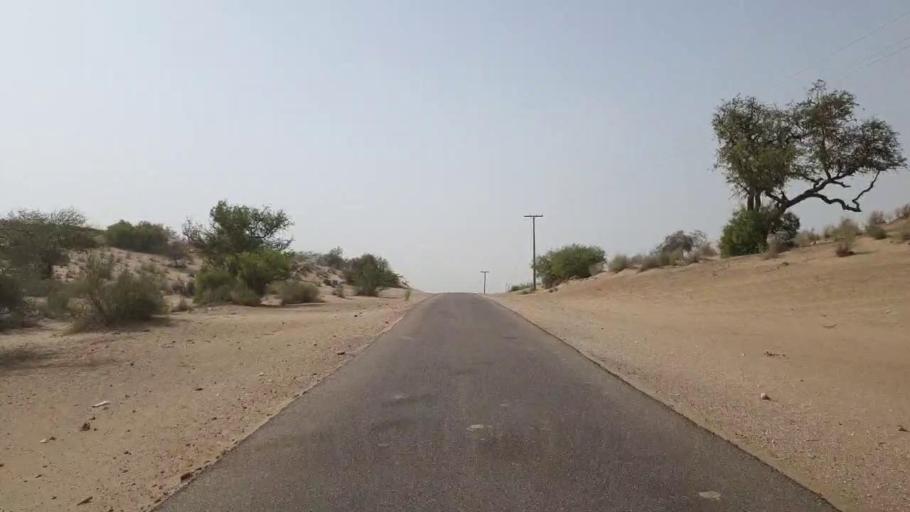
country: PK
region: Sindh
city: Mithi
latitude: 24.5988
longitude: 69.9243
